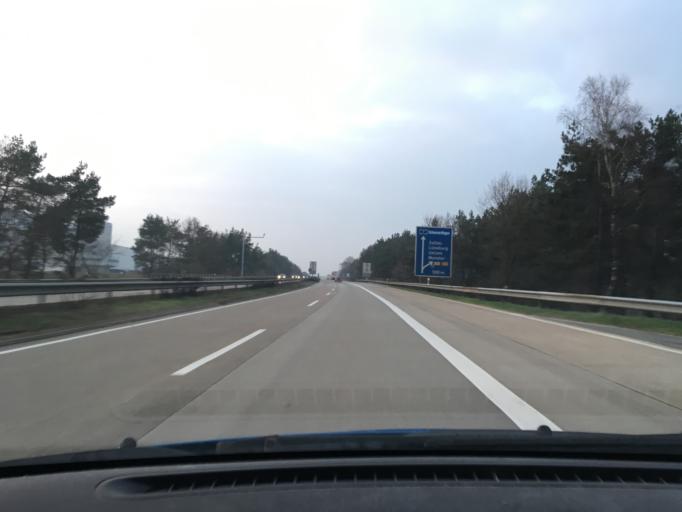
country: DE
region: Lower Saxony
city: Soltau
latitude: 52.9876
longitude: 9.9292
